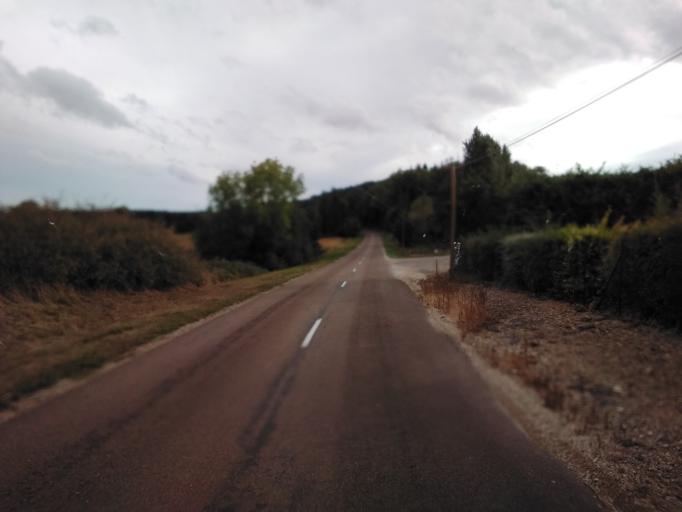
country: FR
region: Champagne-Ardenne
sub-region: Departement de l'Aube
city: Les Riceys
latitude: 47.9750
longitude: 4.3562
